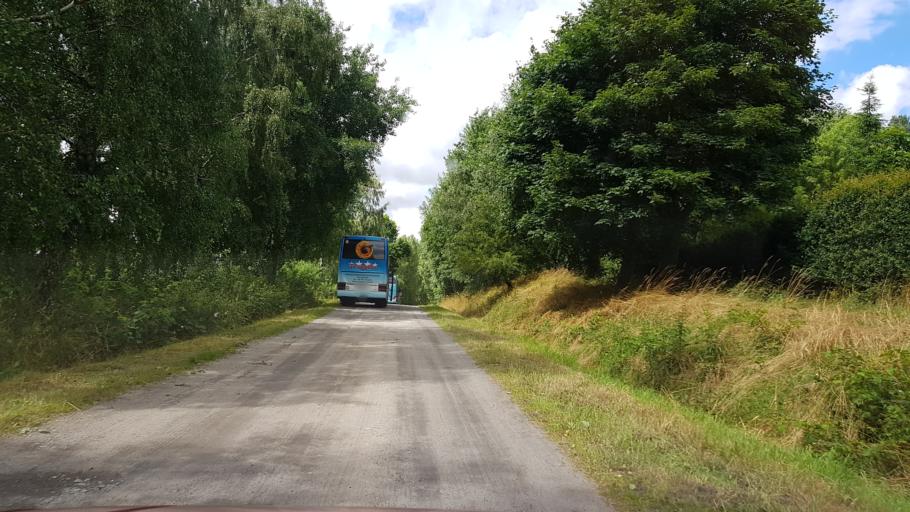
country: PL
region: West Pomeranian Voivodeship
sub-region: Powiat bialogardzki
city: Karlino
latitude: 54.1651
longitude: 15.9267
